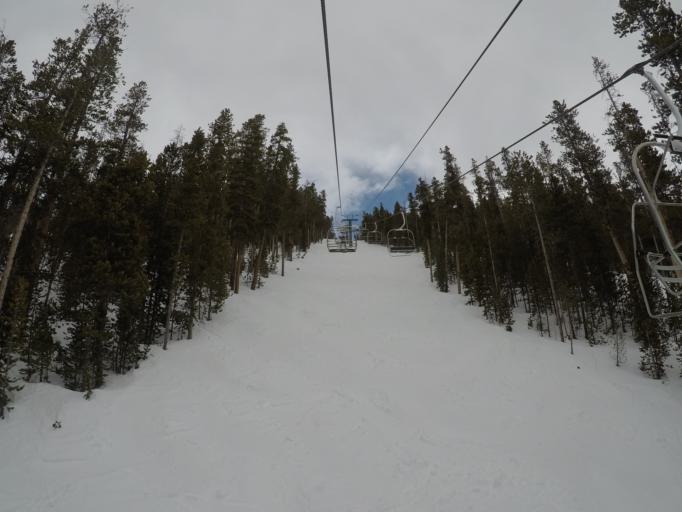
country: US
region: Montana
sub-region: Granite County
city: Philipsburg
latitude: 46.2578
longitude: -113.2448
